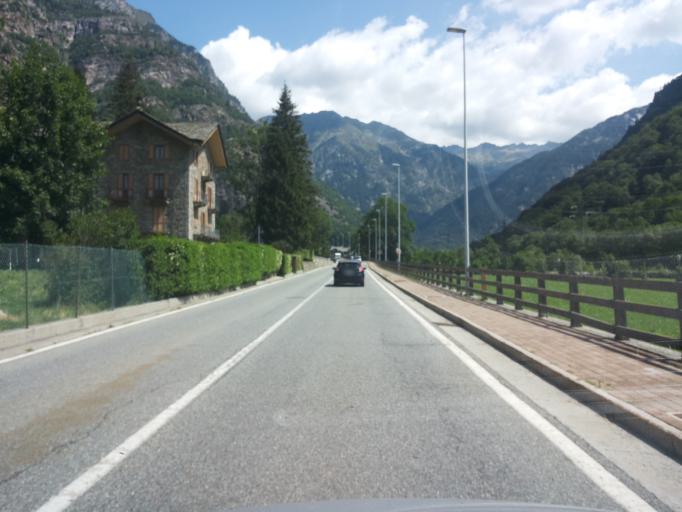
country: IT
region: Aosta Valley
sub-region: Valle d'Aosta
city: Issime
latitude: 45.6881
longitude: 7.8543
